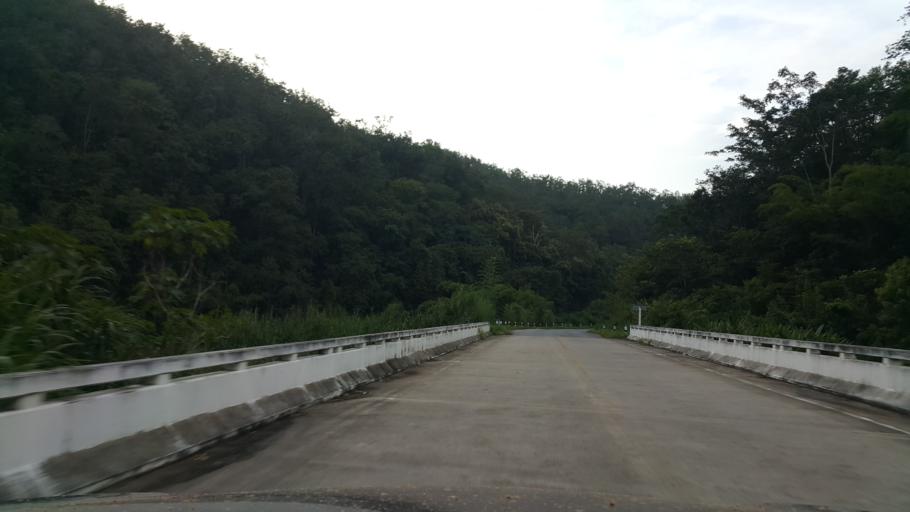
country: TH
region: Mae Hong Son
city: Mae Hi
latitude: 19.2037
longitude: 98.4315
